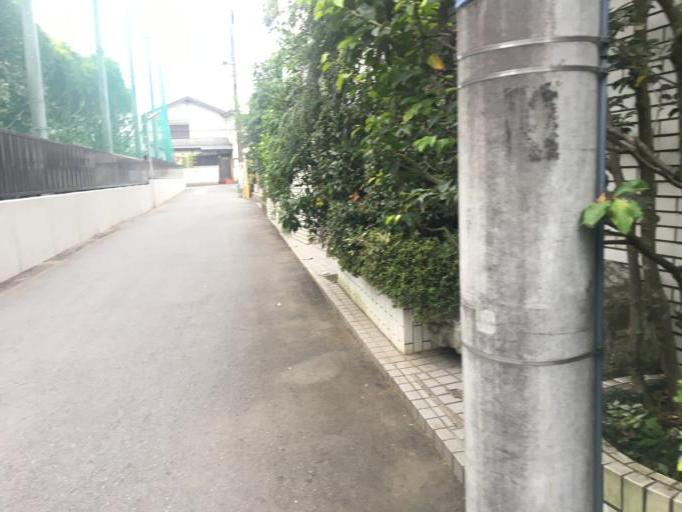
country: JP
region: Saitama
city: Shiki
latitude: 35.8219
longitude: 139.5789
